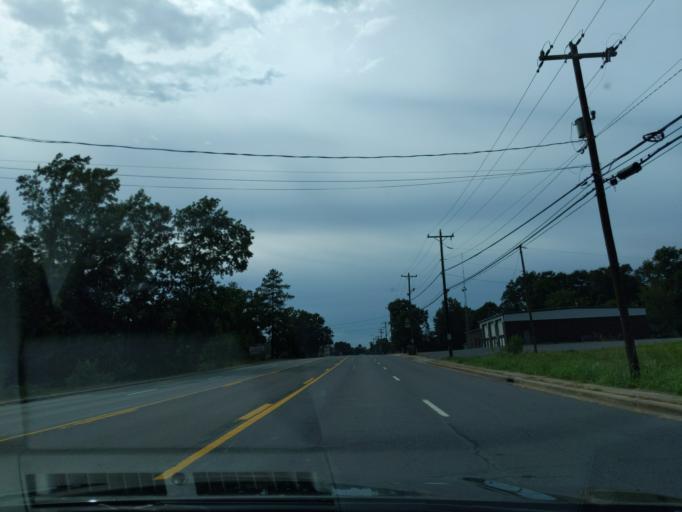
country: US
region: North Carolina
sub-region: Stanly County
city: Albemarle
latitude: 35.4698
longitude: -80.2637
